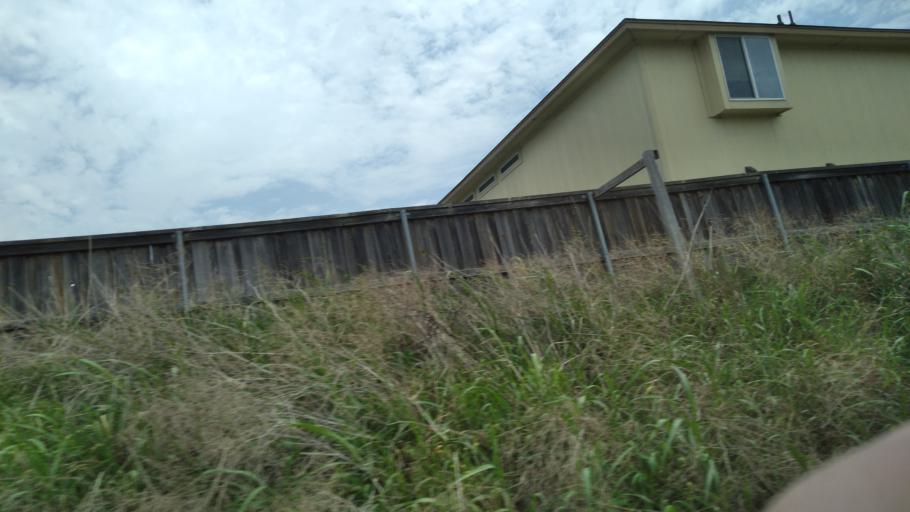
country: US
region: Texas
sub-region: McLennan County
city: Hewitt
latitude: 31.4788
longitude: -97.1627
